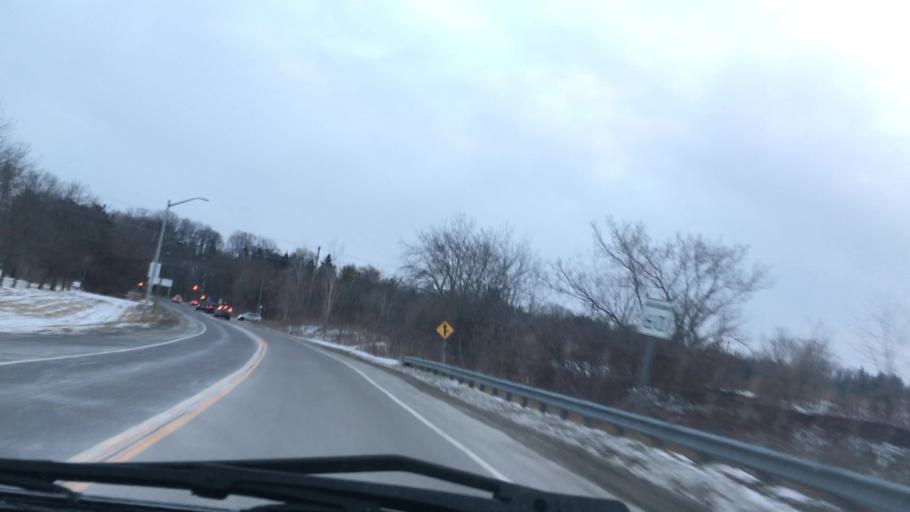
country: CA
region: Ontario
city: Ancaster
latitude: 43.2698
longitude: -79.9370
